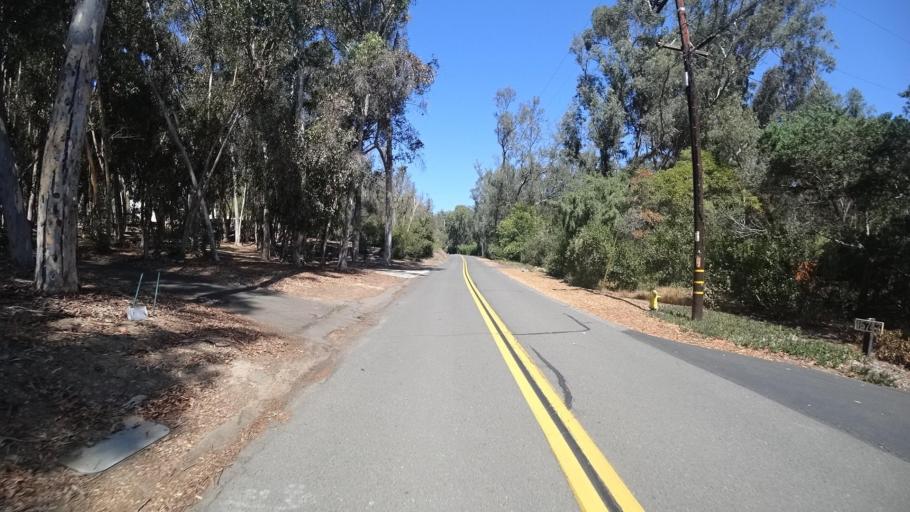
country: US
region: California
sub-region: San Diego County
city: Rancho Santa Fe
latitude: 32.9994
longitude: -117.2151
